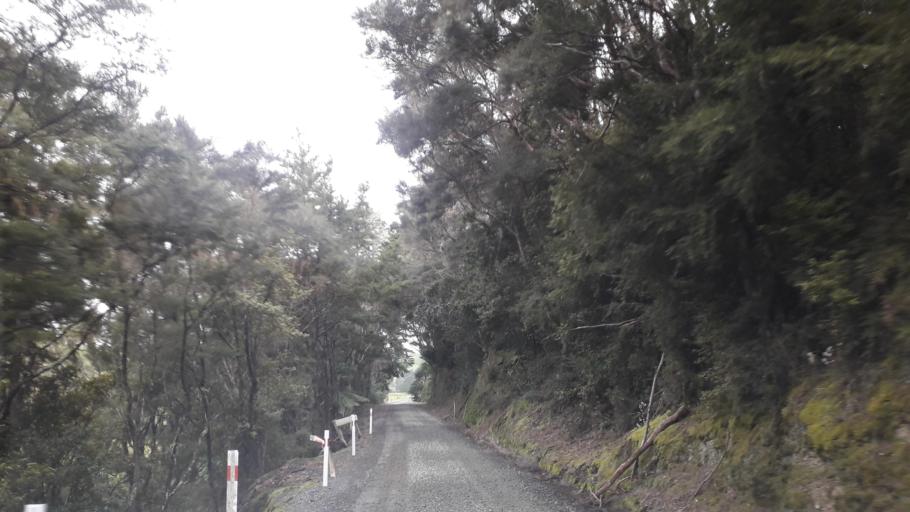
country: NZ
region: Northland
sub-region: Far North District
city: Waimate North
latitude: -35.1488
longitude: 173.7124
